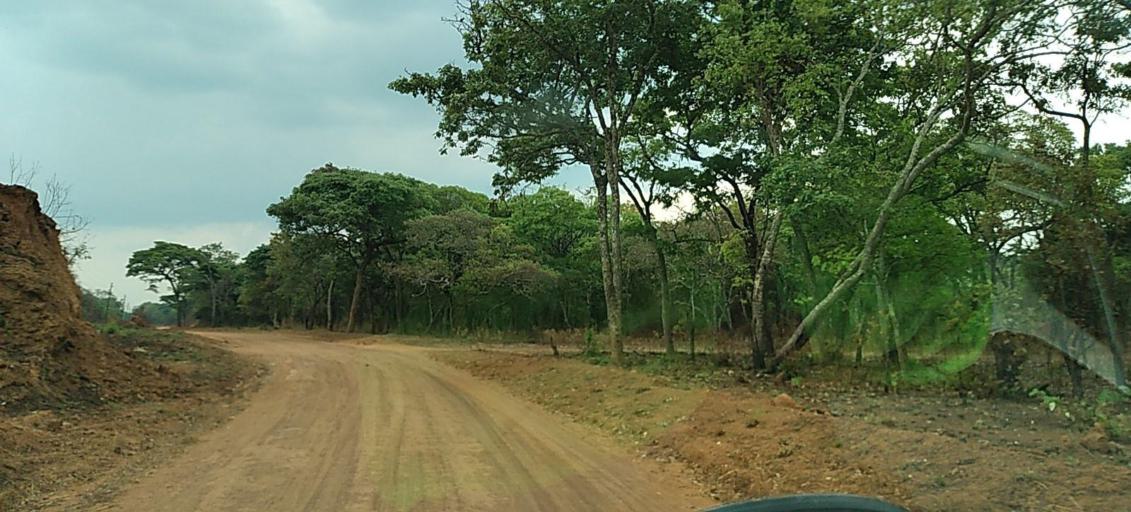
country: ZM
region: North-Western
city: Solwezi
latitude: -12.7812
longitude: 26.4926
